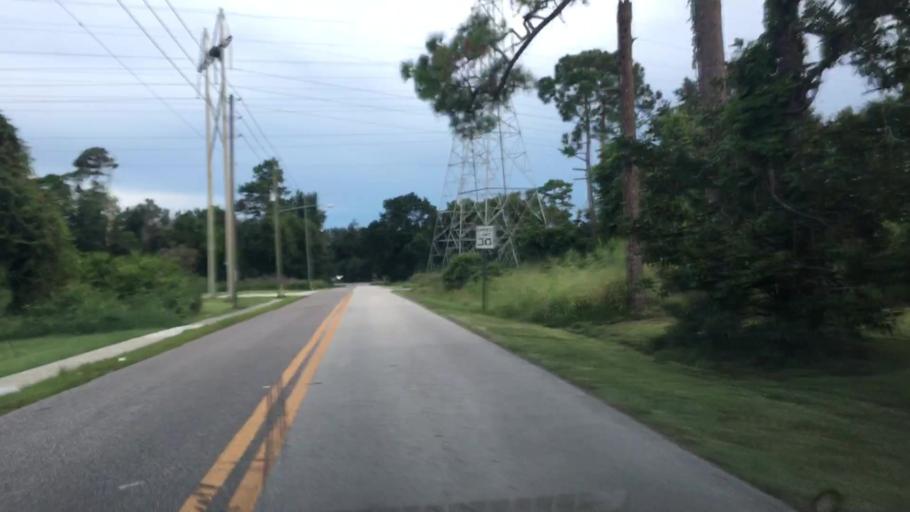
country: US
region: Florida
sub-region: Volusia County
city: DeBary
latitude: 28.8731
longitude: -81.2880
